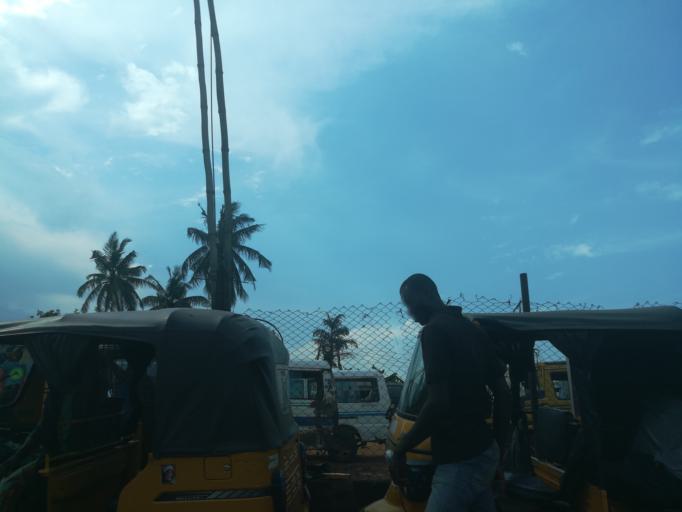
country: NG
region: Lagos
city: Ikorodu
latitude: 6.6275
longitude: 3.5079
